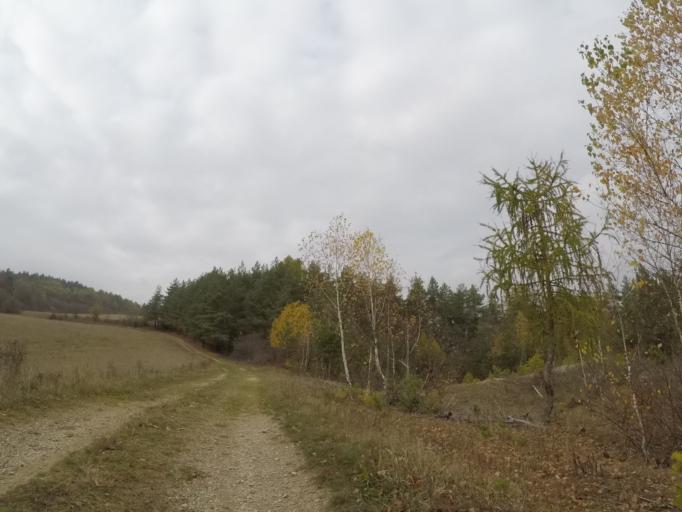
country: SK
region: Presovsky
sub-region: Okres Presov
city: Presov
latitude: 48.9036
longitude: 21.1739
